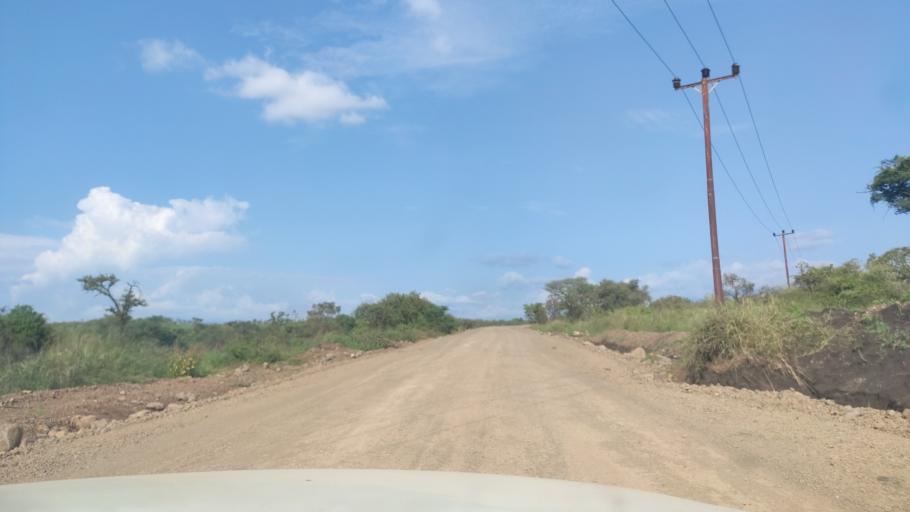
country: ET
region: Southern Nations, Nationalities, and People's Region
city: Felege Neway
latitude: 6.4282
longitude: 37.2091
